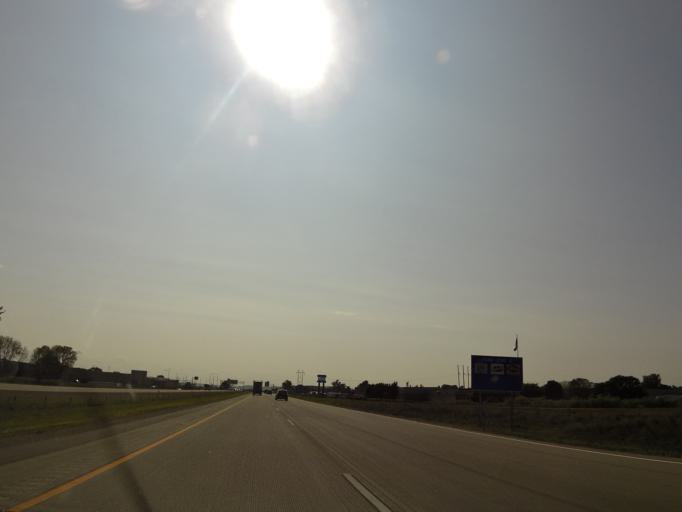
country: US
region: Wisconsin
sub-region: La Crosse County
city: Onalaska
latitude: 43.8735
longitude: -91.2110
